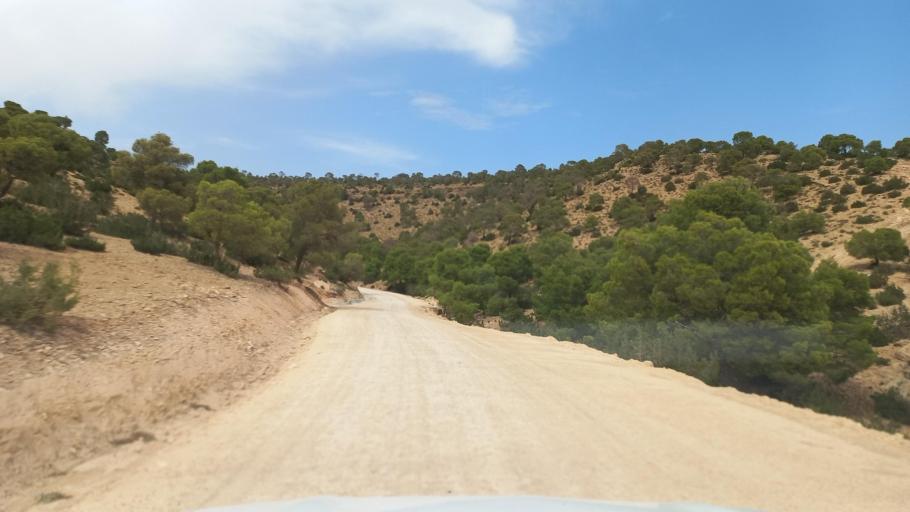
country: TN
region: Al Qasrayn
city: Kasserine
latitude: 35.3740
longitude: 8.8880
